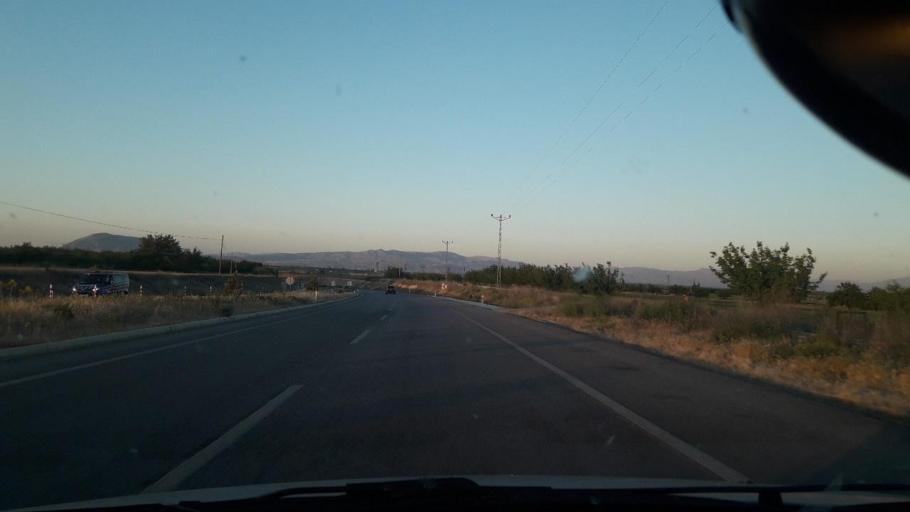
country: TR
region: Malatya
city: Yazihan
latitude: 38.4985
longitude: 38.2280
